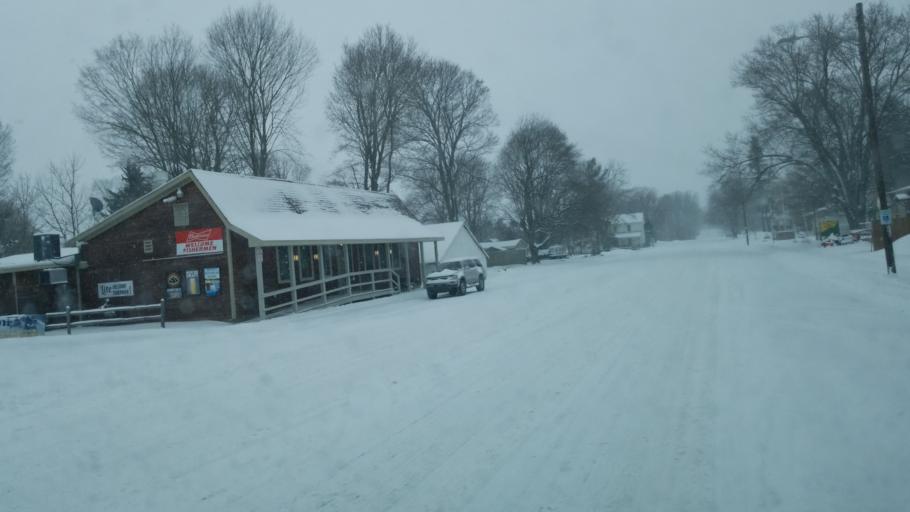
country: US
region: Michigan
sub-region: Osceola County
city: Reed City
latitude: 43.8498
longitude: -85.4445
